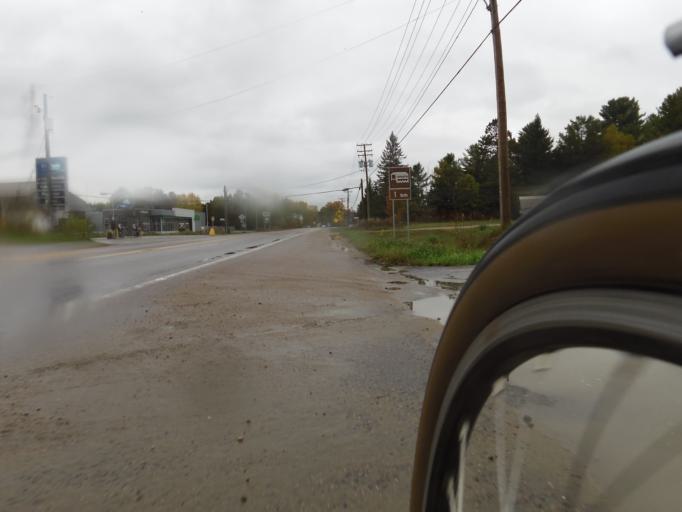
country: CA
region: Quebec
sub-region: Outaouais
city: Fort-Coulonge
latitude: 45.8537
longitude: -76.7355
